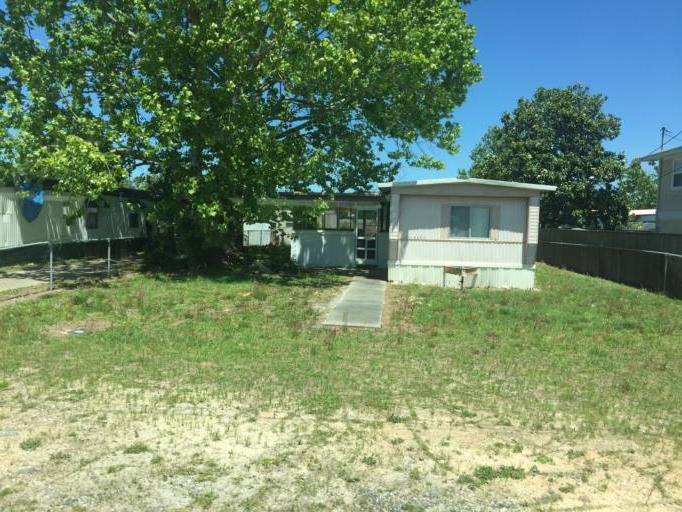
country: US
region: Florida
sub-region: Bay County
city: Laguna Beach
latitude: 30.2428
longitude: -85.9221
